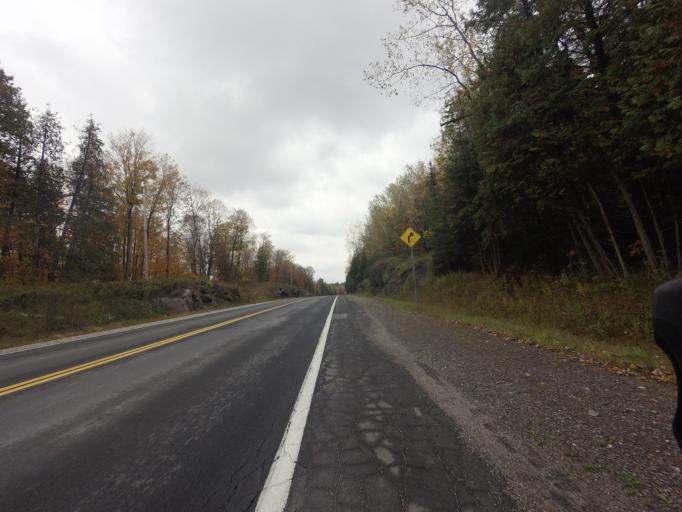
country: CA
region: Ontario
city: Perth
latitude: 45.1144
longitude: -76.4871
